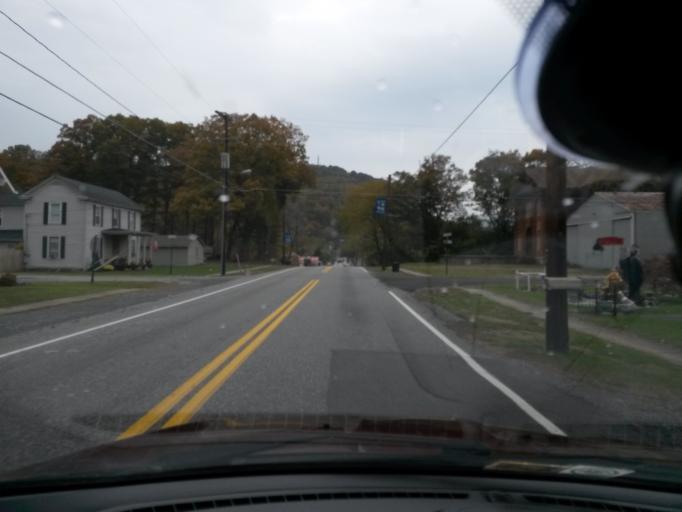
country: US
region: Virginia
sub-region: Alleghany County
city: Clifton Forge
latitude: 37.7959
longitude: -79.7895
